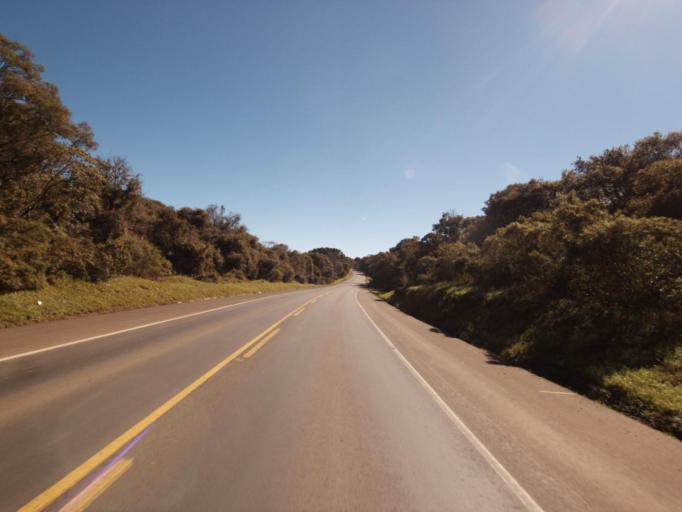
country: BR
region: Santa Catarina
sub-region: Xanxere
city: Xanxere
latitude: -26.8827
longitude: -52.1786
